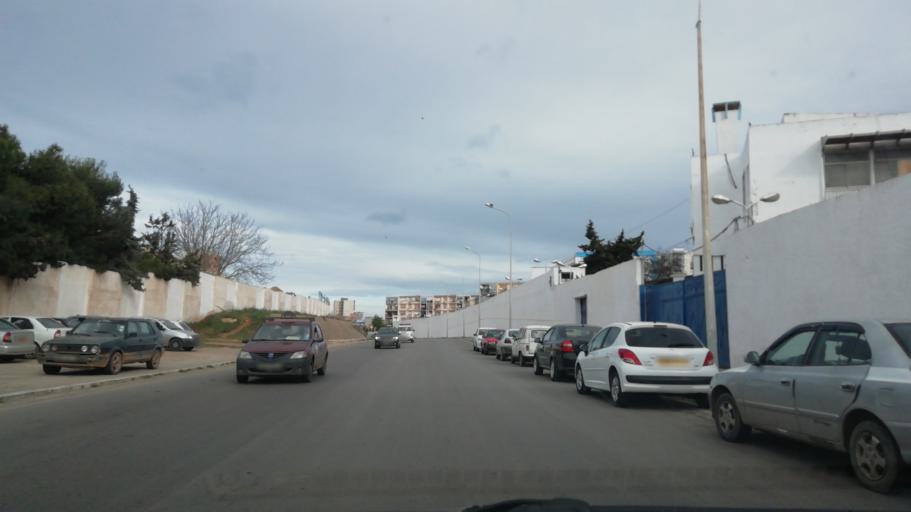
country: DZ
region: Oran
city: Oran
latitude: 35.6991
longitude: -0.6133
